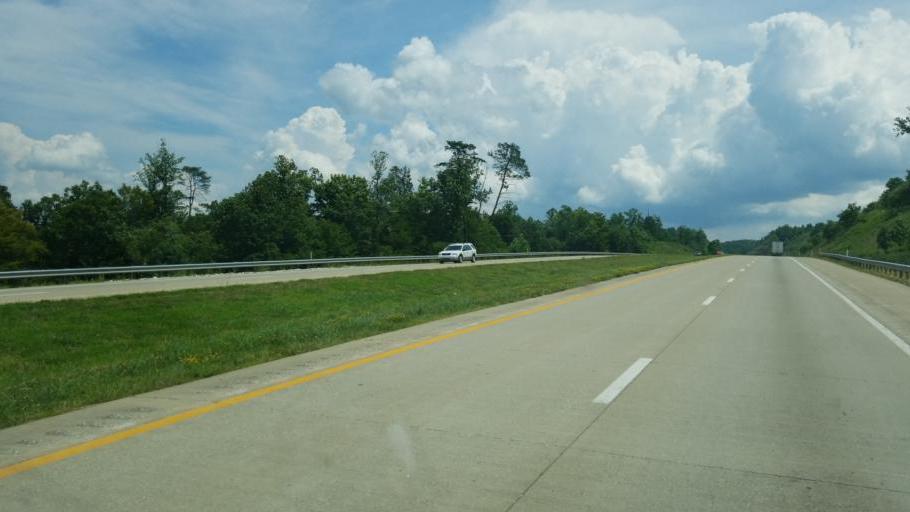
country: US
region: West Virginia
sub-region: Putnam County
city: Eleanor
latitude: 38.5369
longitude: -81.9595
